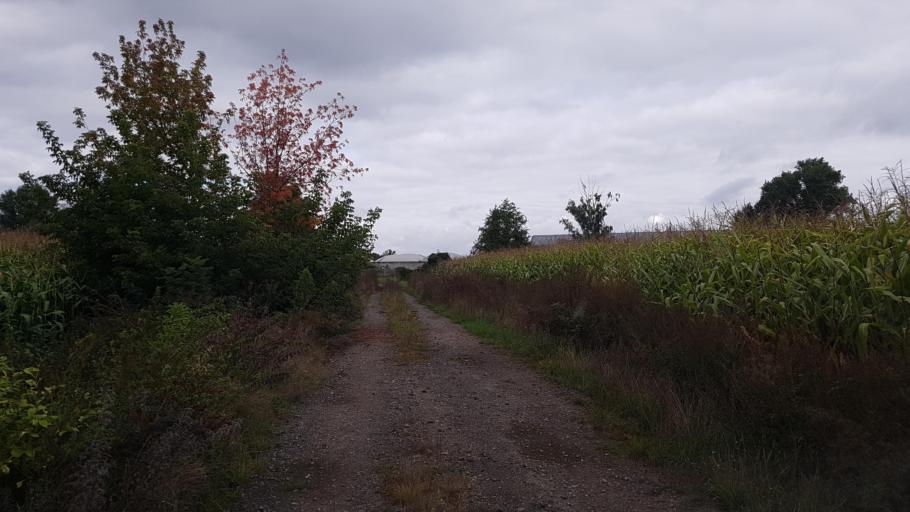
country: DE
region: Brandenburg
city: Tettau
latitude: 51.4629
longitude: 13.7315
